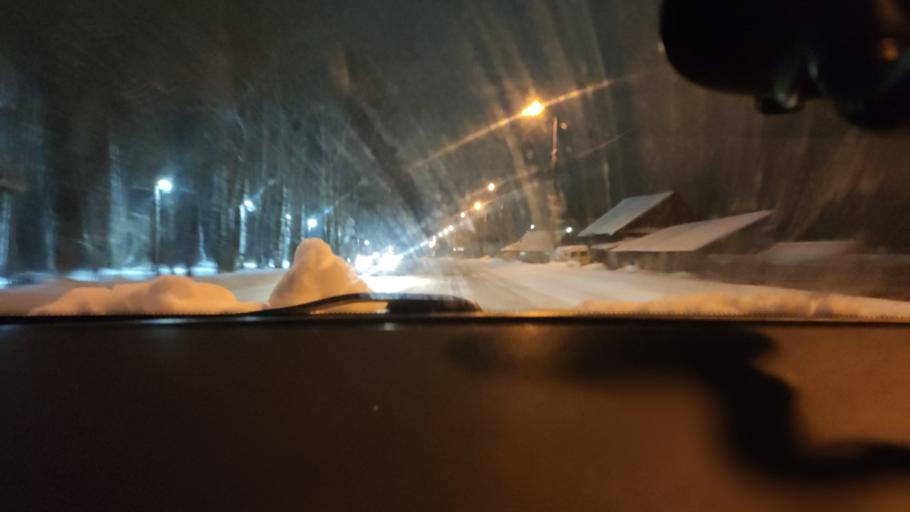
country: RU
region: Perm
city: Krasnokamsk
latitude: 58.0611
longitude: 55.8089
